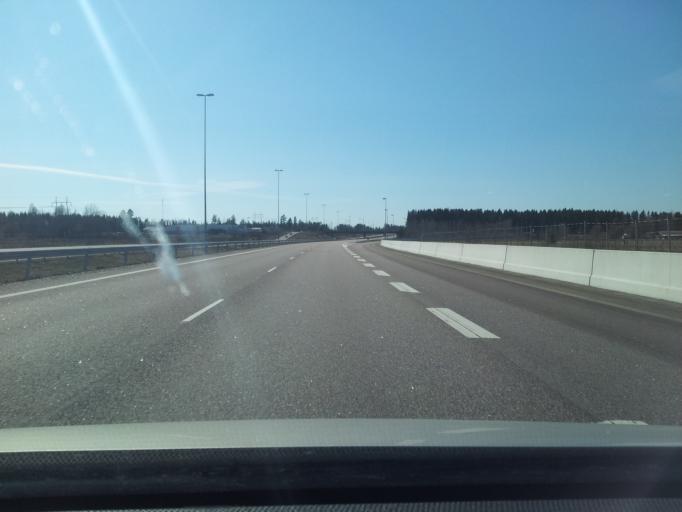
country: FI
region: Uusimaa
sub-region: Loviisa
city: Lovisa
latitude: 60.4627
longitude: 26.2021
